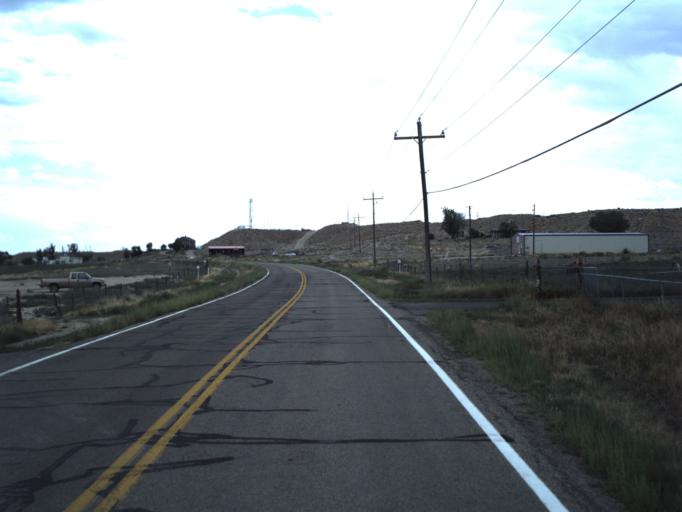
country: US
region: Utah
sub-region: Emery County
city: Huntington
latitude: 39.3744
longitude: -110.8524
